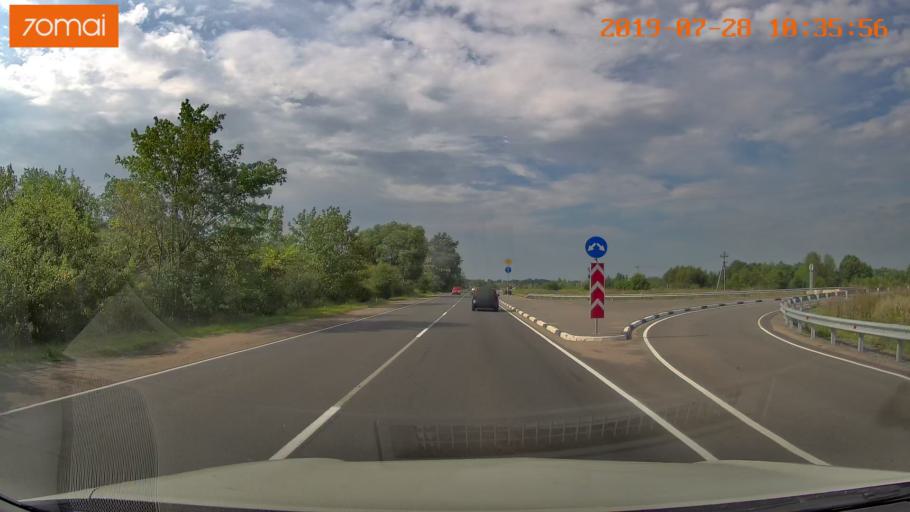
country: RU
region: Kaliningrad
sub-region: Gorod Kaliningrad
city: Kaliningrad
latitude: 54.7420
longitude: 20.4266
